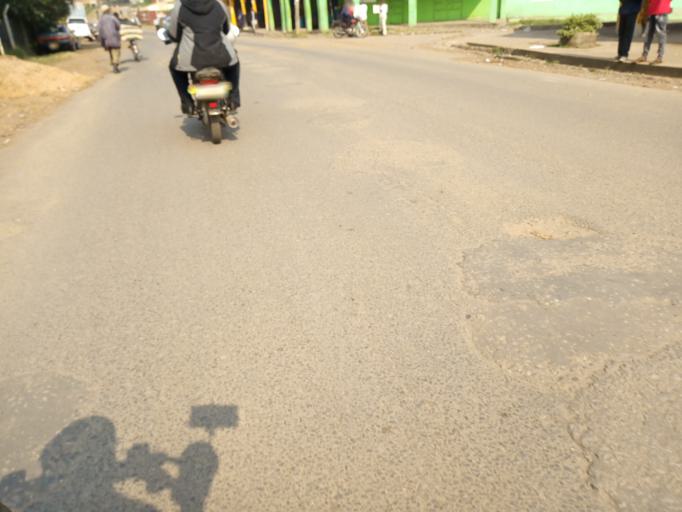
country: UG
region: Western Region
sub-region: Kisoro District
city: Kisoro
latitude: -1.2818
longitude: 29.6922
